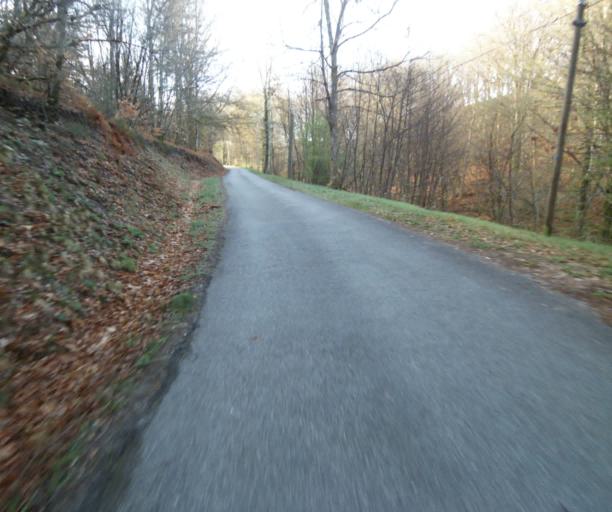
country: FR
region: Limousin
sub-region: Departement de la Correze
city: Correze
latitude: 45.2946
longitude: 1.8481
